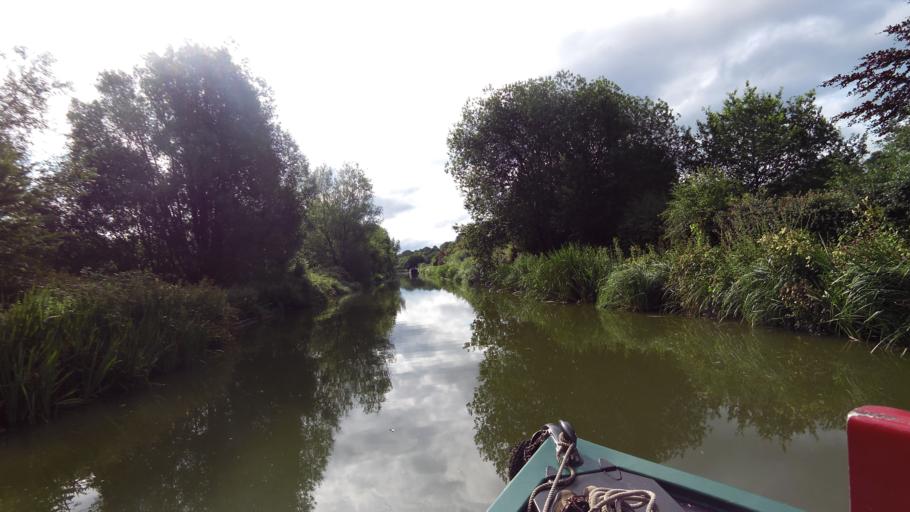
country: GB
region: England
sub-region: West Berkshire
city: Hungerford
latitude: 51.4142
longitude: -1.5073
